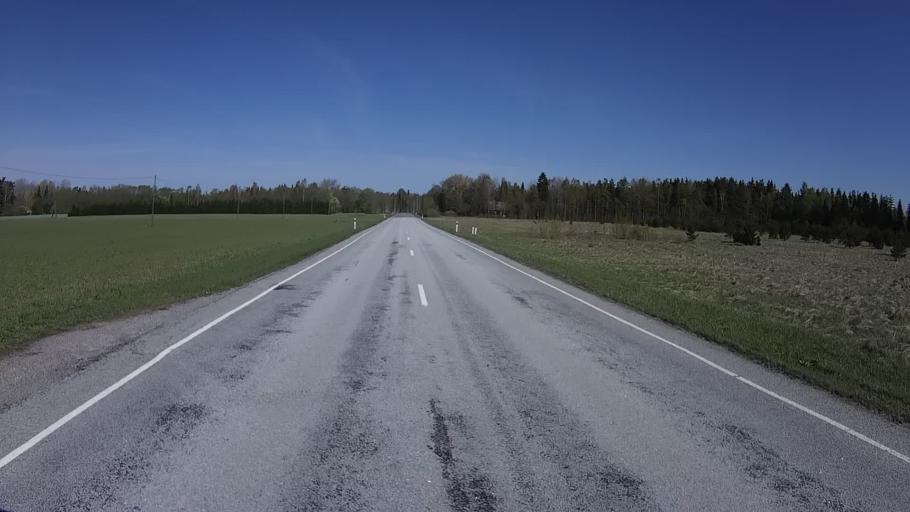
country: EE
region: Raplamaa
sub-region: Jaervakandi vald
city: Jarvakandi
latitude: 58.8176
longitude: 24.8025
